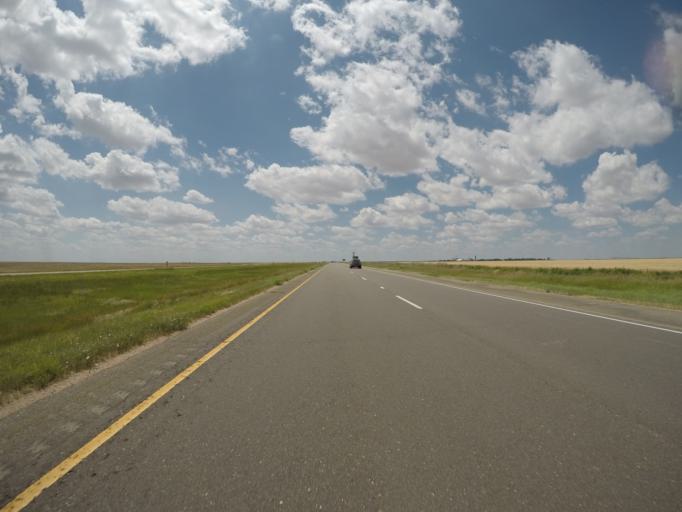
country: US
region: Colorado
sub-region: Kit Carson County
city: Burlington
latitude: 39.2943
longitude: -102.4017
